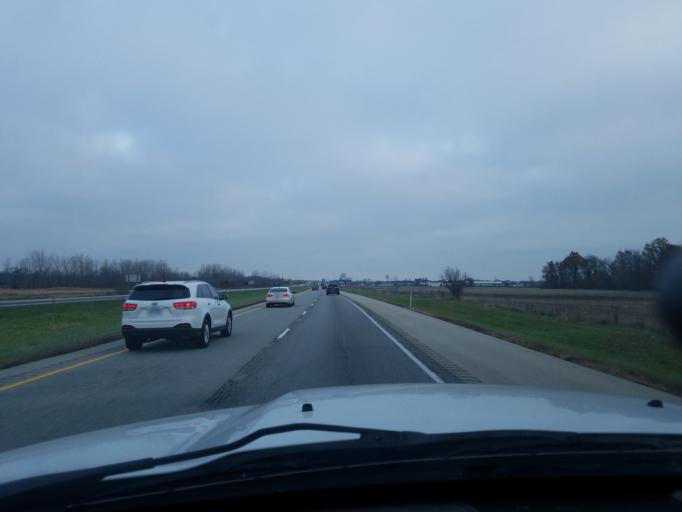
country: US
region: Indiana
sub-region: Delaware County
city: Daleville
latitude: 40.1012
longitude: -85.5689
